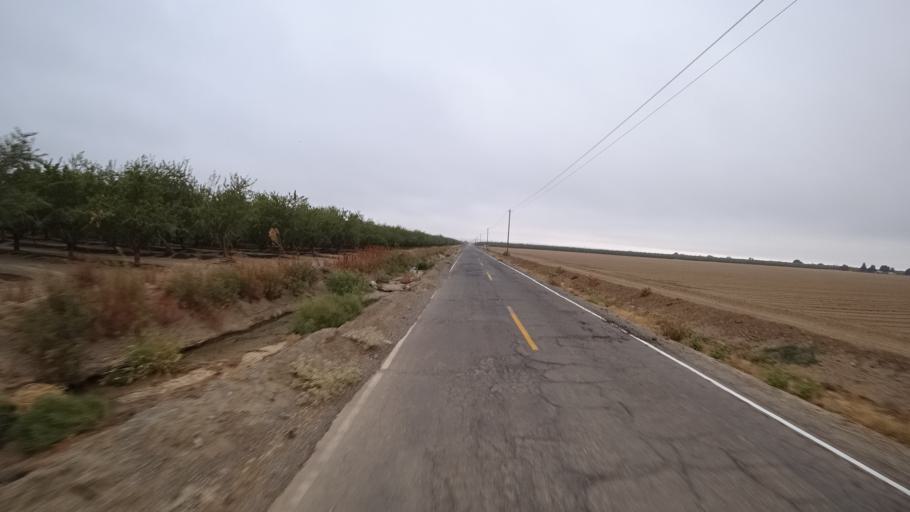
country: US
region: California
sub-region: Yolo County
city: Dunnigan
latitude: 38.9258
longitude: -122.0457
